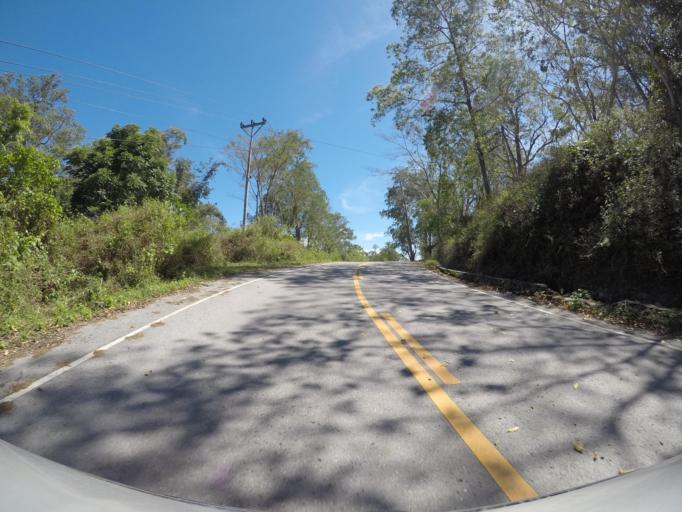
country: TL
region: Manufahi
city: Same
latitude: -8.8949
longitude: 125.9825
